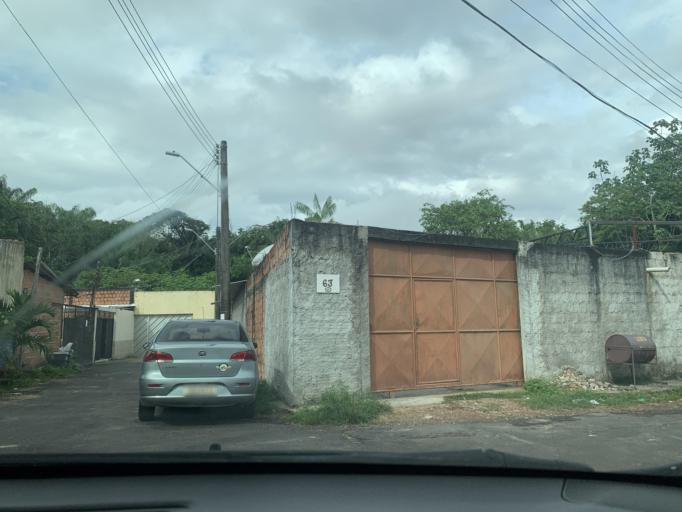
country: BR
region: Amazonas
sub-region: Manaus
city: Manaus
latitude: -3.0894
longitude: -59.9764
